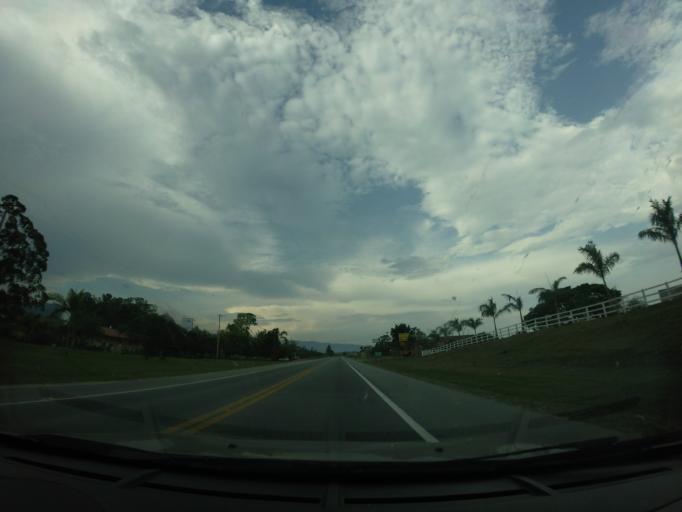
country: BR
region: Sao Paulo
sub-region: Tremembe
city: Tremembe
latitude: -22.9767
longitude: -45.6461
